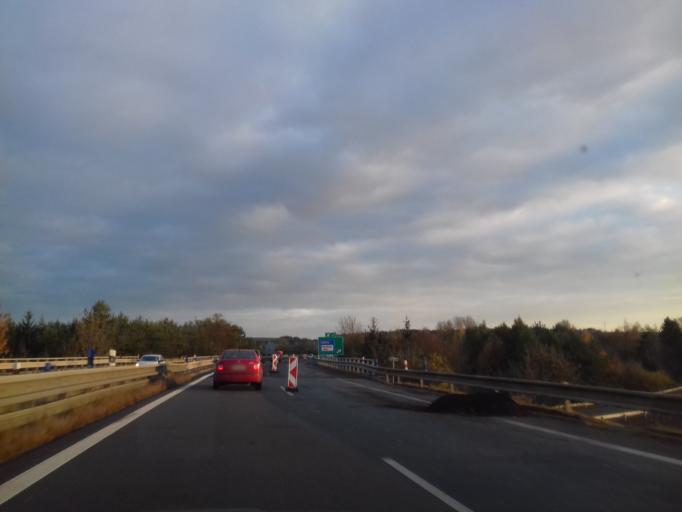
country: CZ
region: Olomoucky
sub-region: Okres Prostejov
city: Prostejov
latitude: 49.4812
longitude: 17.1307
